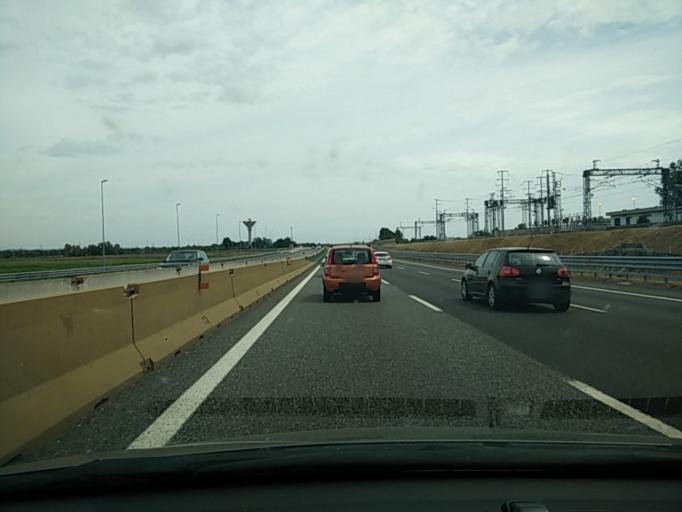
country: IT
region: Piedmont
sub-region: Provincia di Torino
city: Brandizzo
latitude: 45.1785
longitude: 7.8224
